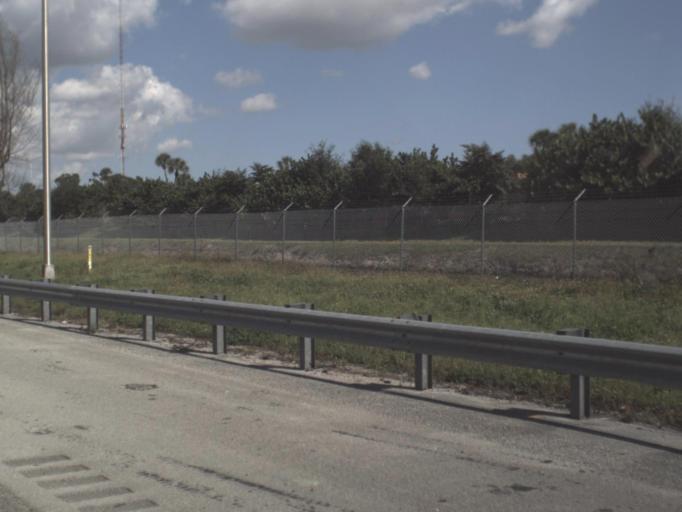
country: US
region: Florida
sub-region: Palm Beach County
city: Villages of Oriole
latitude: 26.5136
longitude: -80.1725
